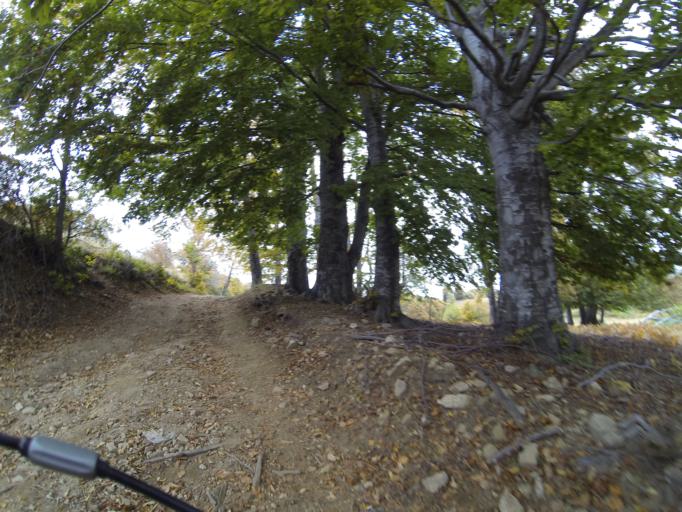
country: RO
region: Gorj
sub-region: Comuna Pades
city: Closani
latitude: 45.0916
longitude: 22.8387
